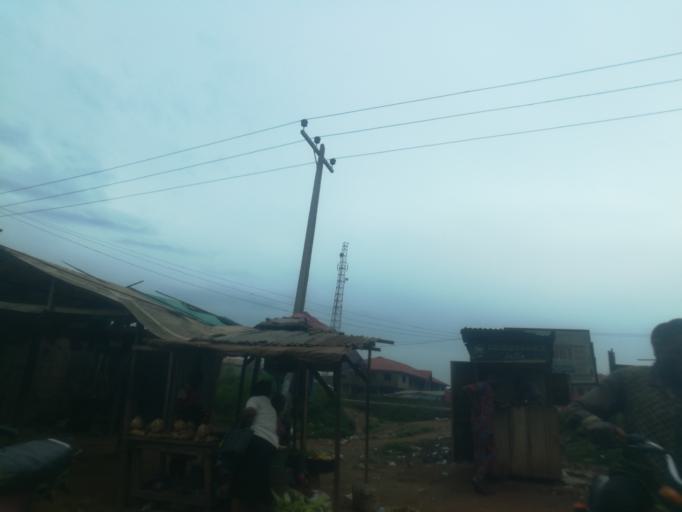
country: NG
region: Oyo
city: Egbeda
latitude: 7.3846
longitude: 3.9883
